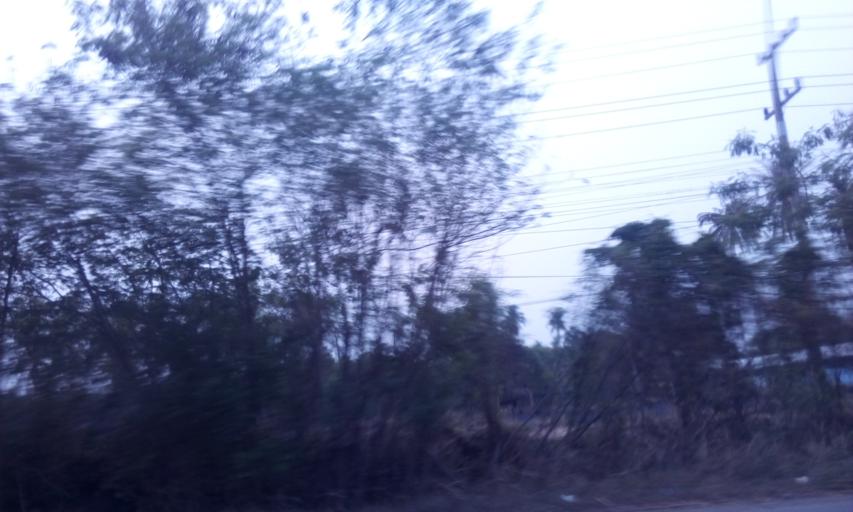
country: TH
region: Chon Buri
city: Ban Bueng
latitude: 13.2350
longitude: 101.2339
